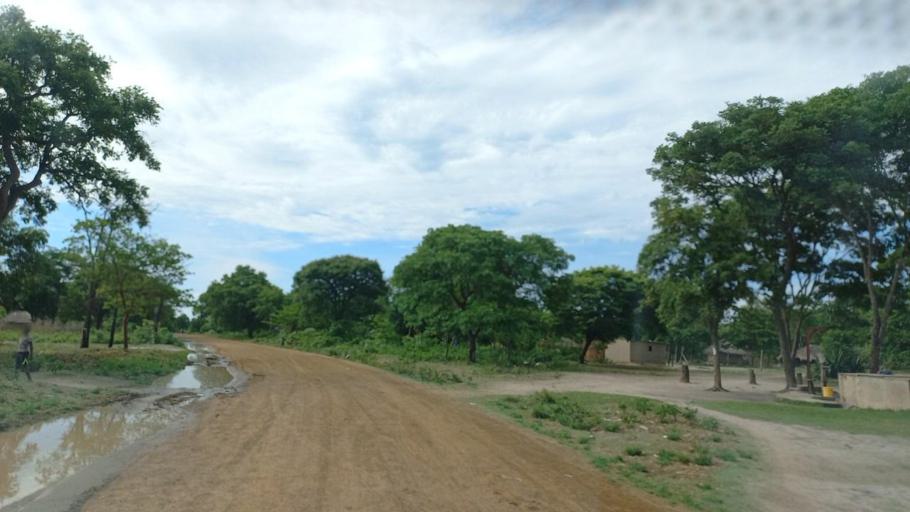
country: ZM
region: North-Western
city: Kabompo
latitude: -13.4607
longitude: 24.4270
